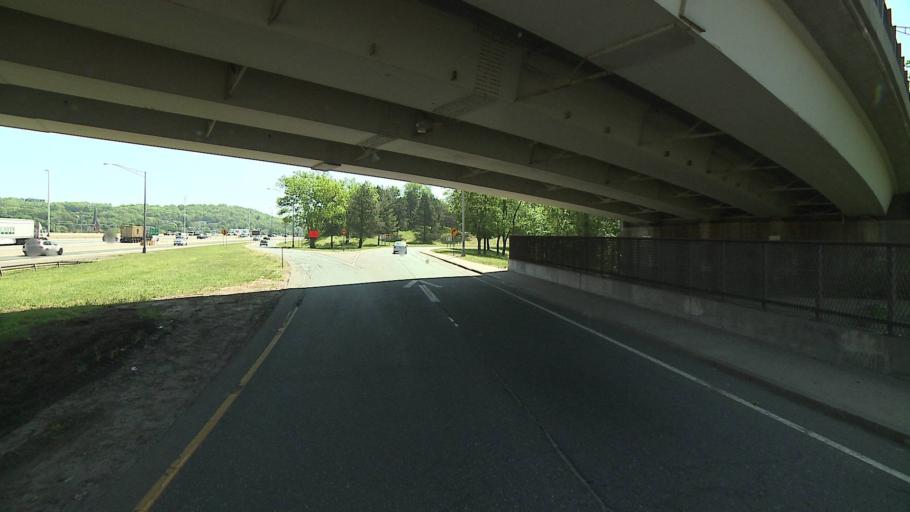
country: US
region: Connecticut
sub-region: New Haven County
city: Waterbury
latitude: 41.5511
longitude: -73.0353
